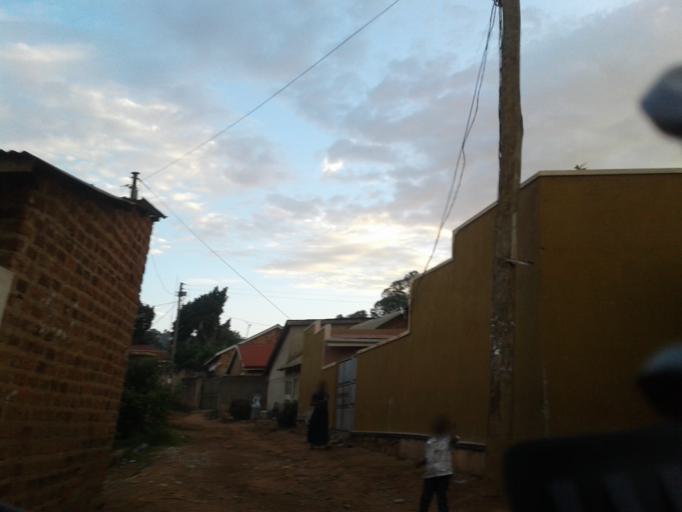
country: UG
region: Central Region
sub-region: Kampala District
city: Kampala
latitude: 0.2644
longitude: 32.6214
